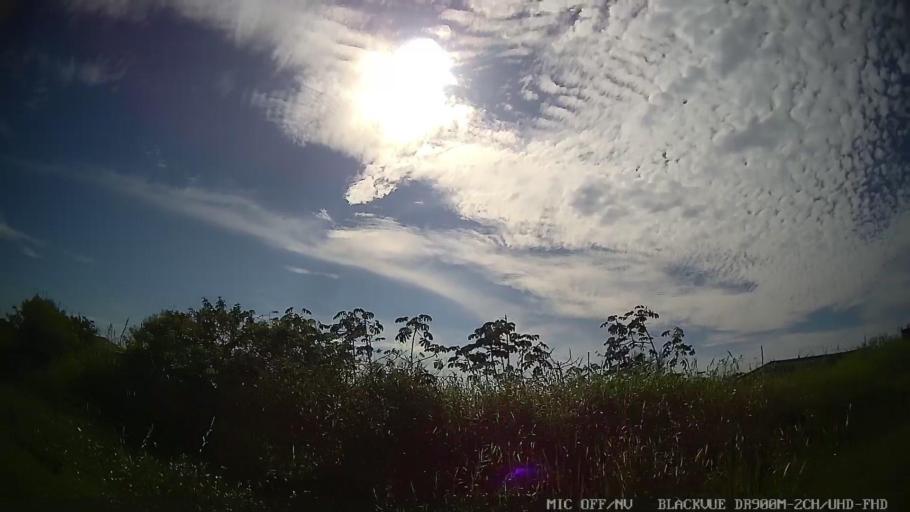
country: BR
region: Sao Paulo
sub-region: Iguape
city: Iguape
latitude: -24.7698
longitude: -47.5888
